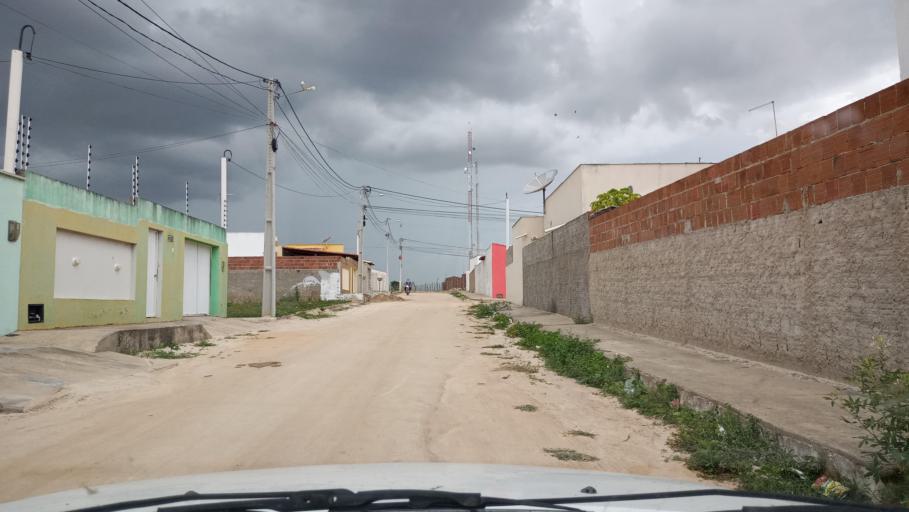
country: BR
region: Rio Grande do Norte
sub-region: Tangara
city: Tangara
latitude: -6.0974
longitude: -35.7152
